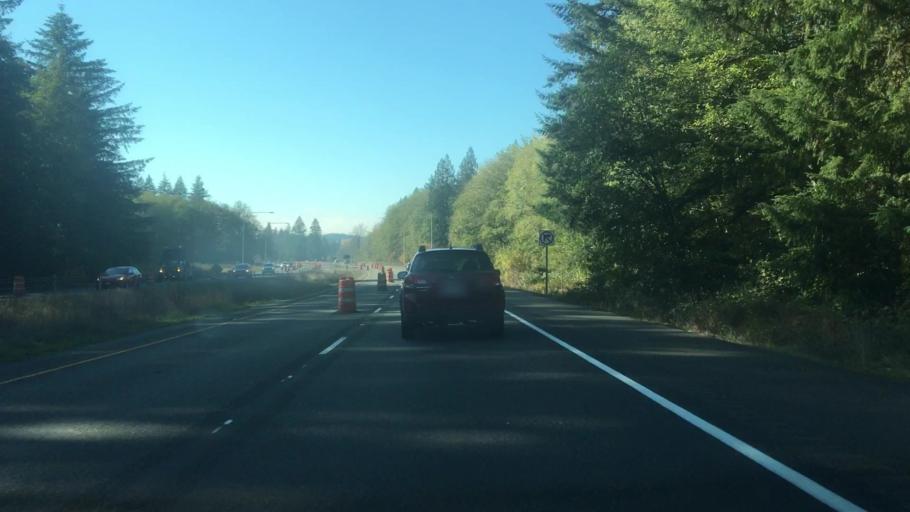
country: US
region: Washington
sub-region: Grays Harbor County
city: McCleary
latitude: 47.0546
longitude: -123.2839
